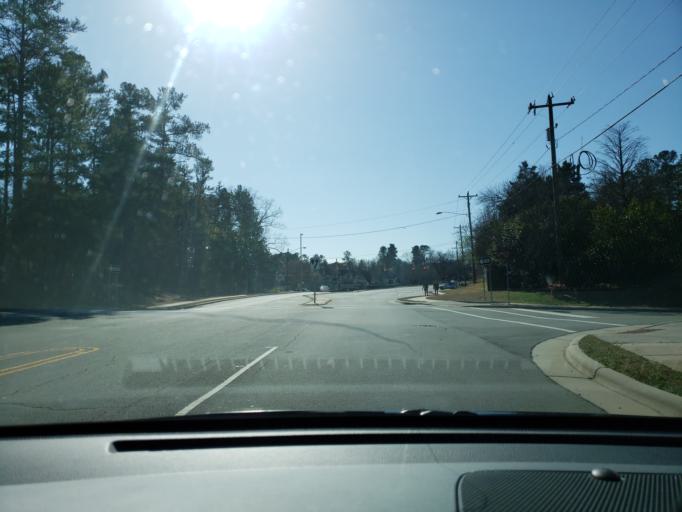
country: US
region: North Carolina
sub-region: Orange County
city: Chapel Hill
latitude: 35.9527
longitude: -79.0159
